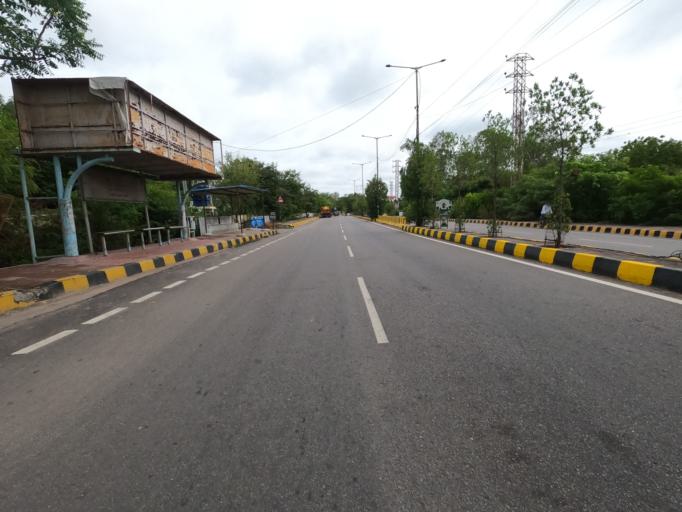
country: IN
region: Telangana
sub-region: Hyderabad
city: Hyderabad
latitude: 17.3330
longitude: 78.4096
